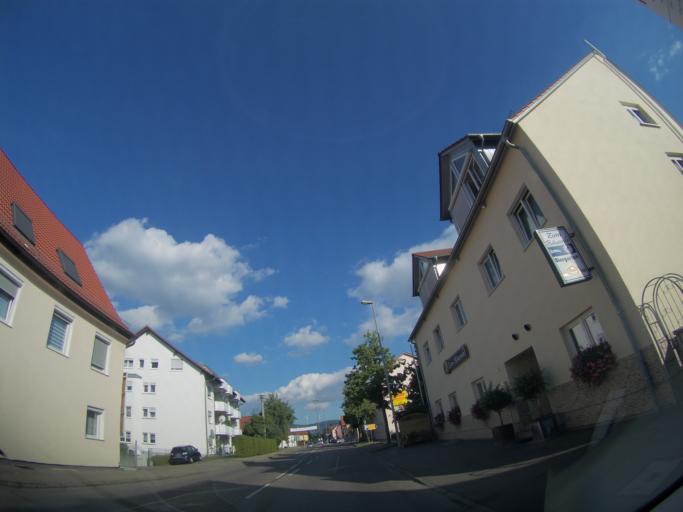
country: DE
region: Baden-Wuerttemberg
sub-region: Regierungsbezirk Stuttgart
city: Sussen
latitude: 48.6766
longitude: 9.7543
